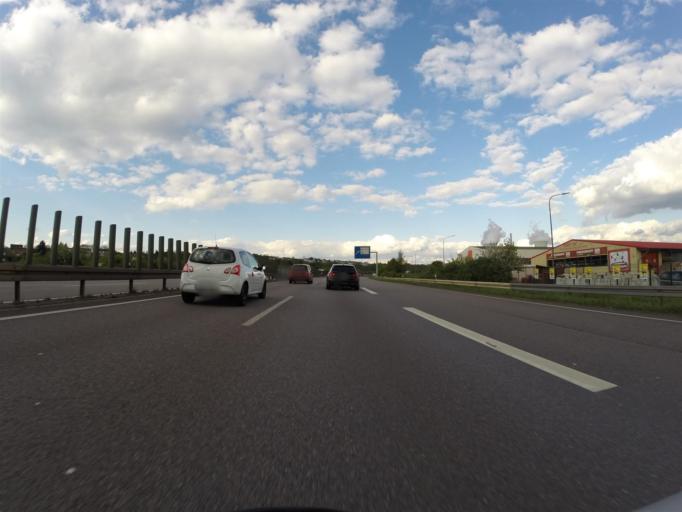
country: DE
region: Saarland
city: Volklingen
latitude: 49.2472
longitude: 6.8643
